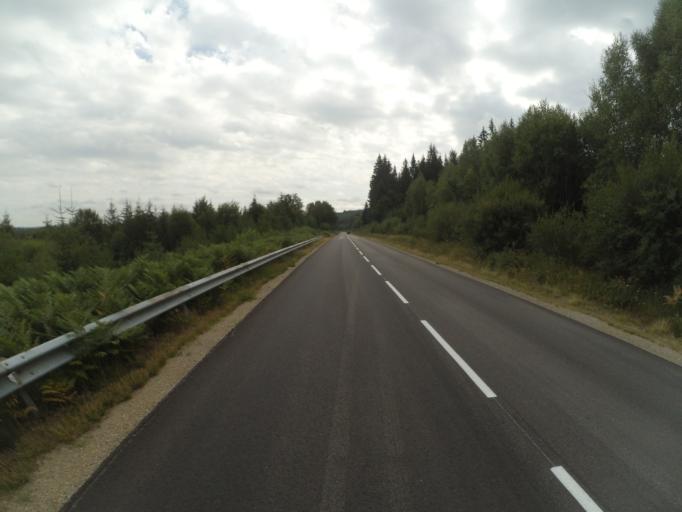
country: FR
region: Limousin
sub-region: Departement de la Creuse
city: La Courtine
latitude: 45.6608
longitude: 2.2116
